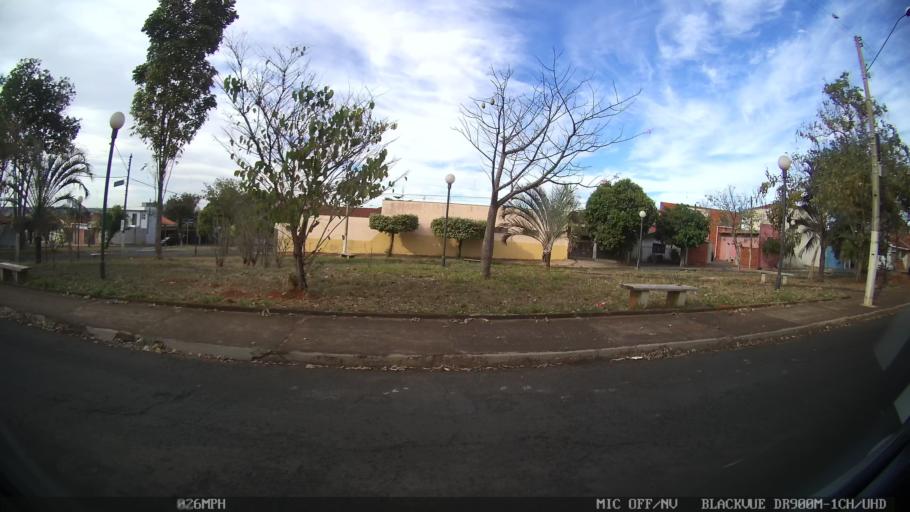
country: BR
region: Sao Paulo
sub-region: Catanduva
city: Catanduva
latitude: -21.1243
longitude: -48.9973
